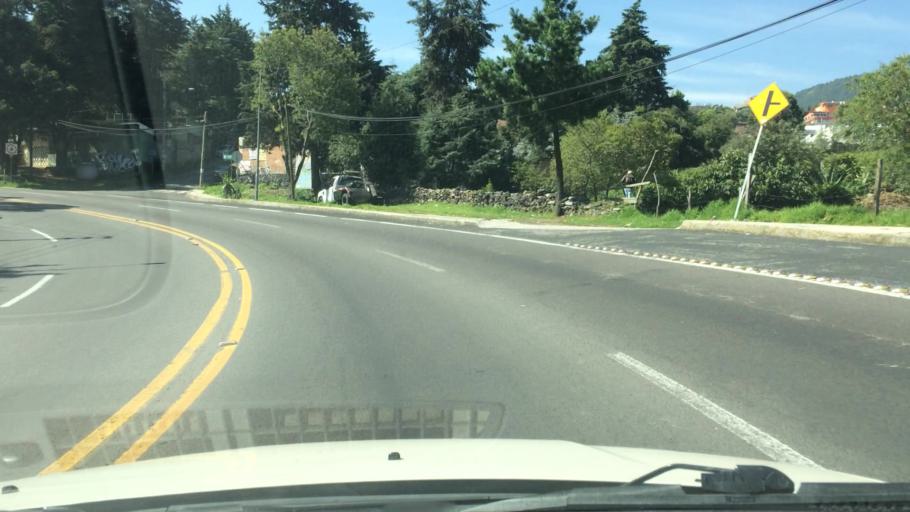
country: MX
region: Mexico City
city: Tlalpan
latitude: 19.2450
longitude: -99.1708
